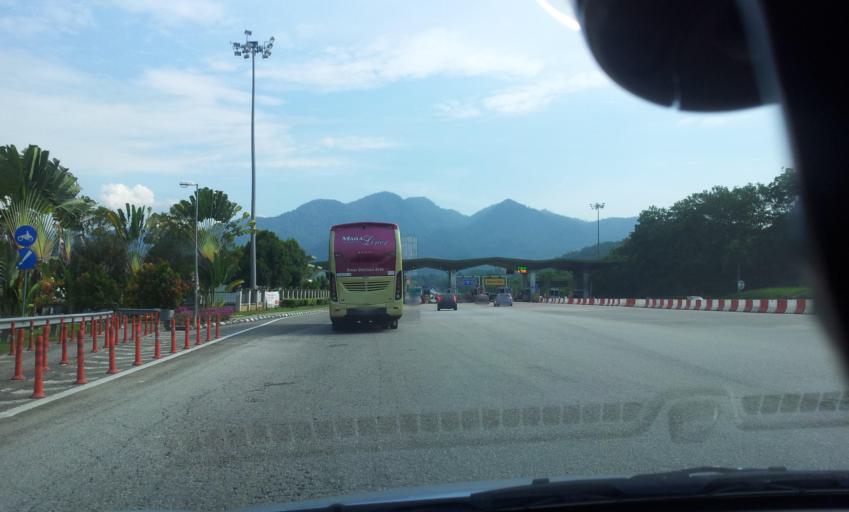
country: MY
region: Pahang
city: Bentong Town
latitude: 3.4449
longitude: 102.0285
